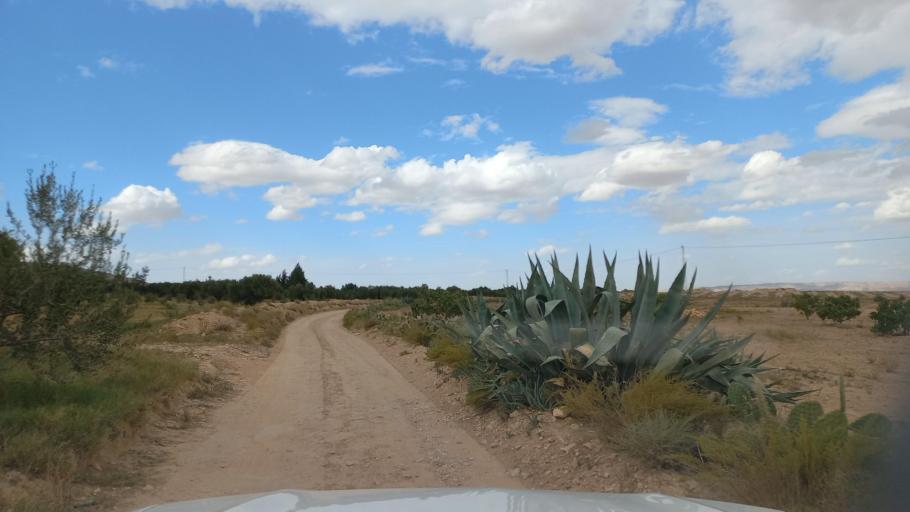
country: TN
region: Al Qasrayn
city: Sbiba
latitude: 35.4394
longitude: 9.0999
